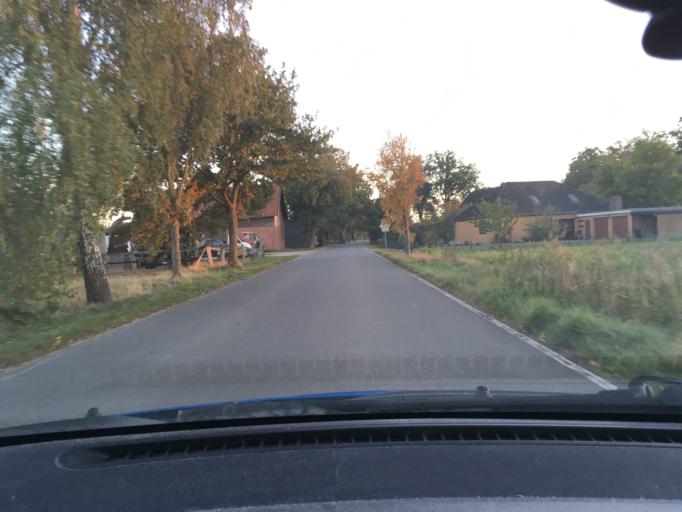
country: DE
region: Lower Saxony
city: Ludersburg
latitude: 53.3090
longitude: 10.6164
